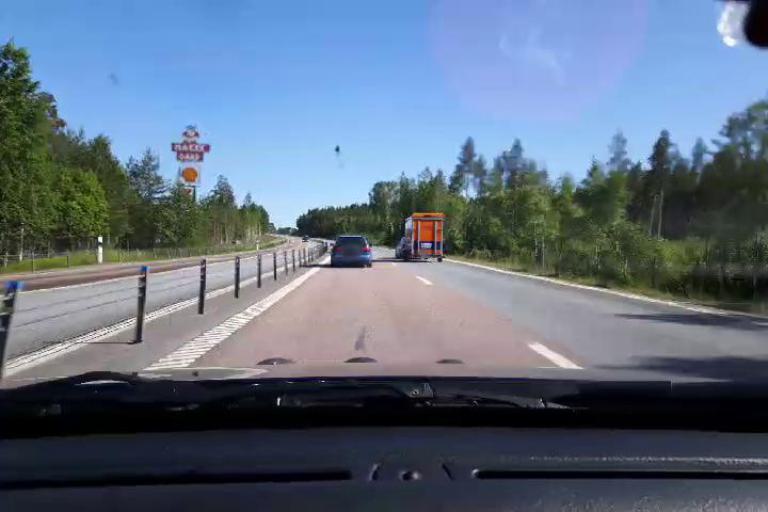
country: SE
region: Gaevleborg
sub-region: Gavle Kommun
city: Norrsundet
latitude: 60.8998
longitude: 17.0205
